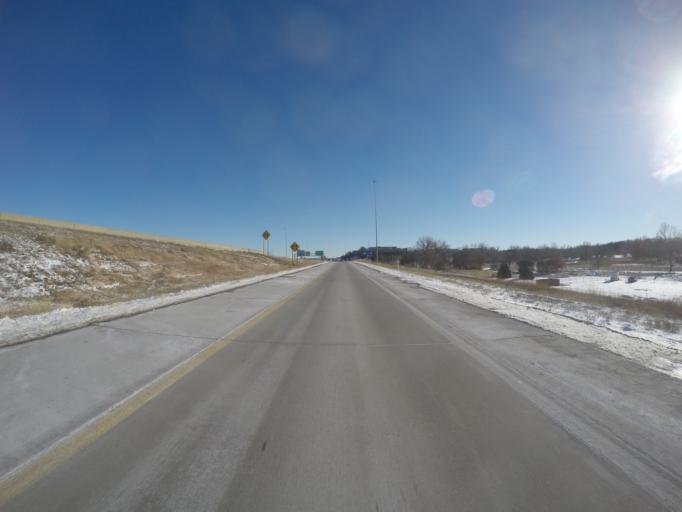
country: US
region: Kansas
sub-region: Shawnee County
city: Topeka
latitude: 39.0503
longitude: -95.7728
